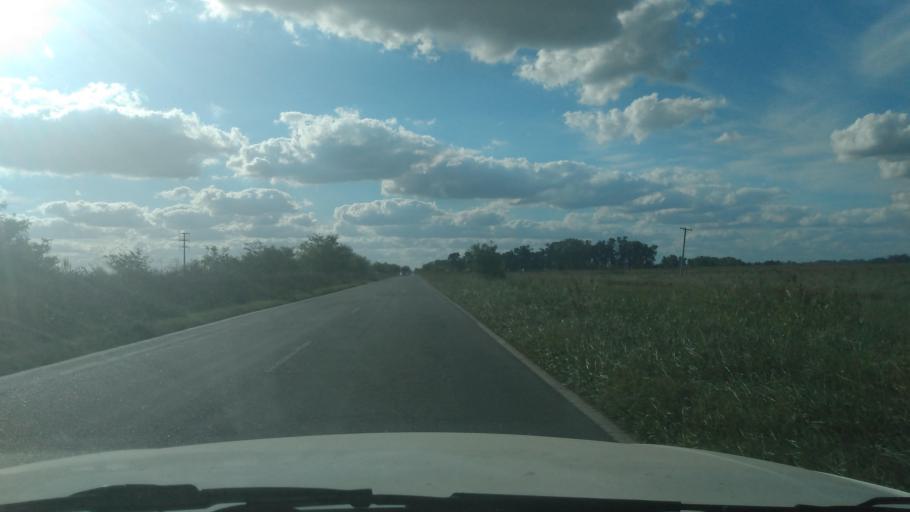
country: AR
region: Buenos Aires
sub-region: Partido de Mercedes
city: Mercedes
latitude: -34.7661
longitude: -59.3734
